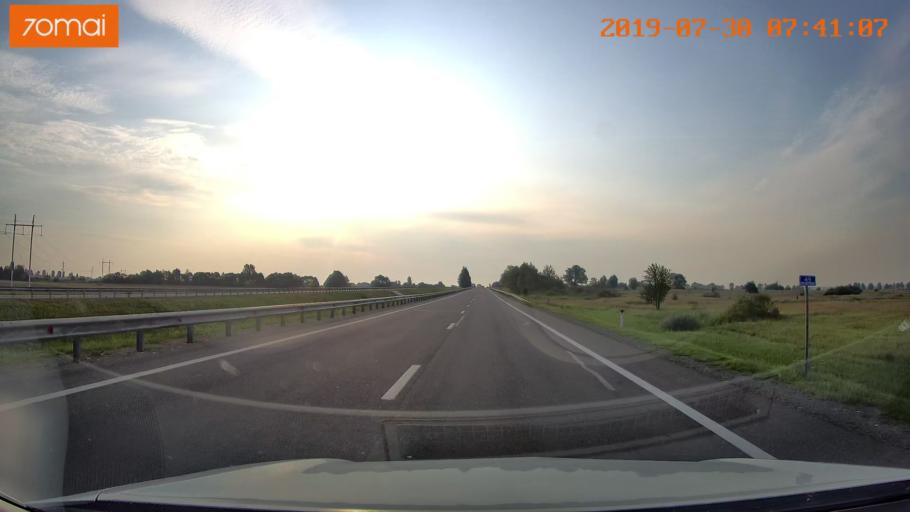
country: RU
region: Kaliningrad
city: Gvardeysk
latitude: 54.6485
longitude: 21.2428
